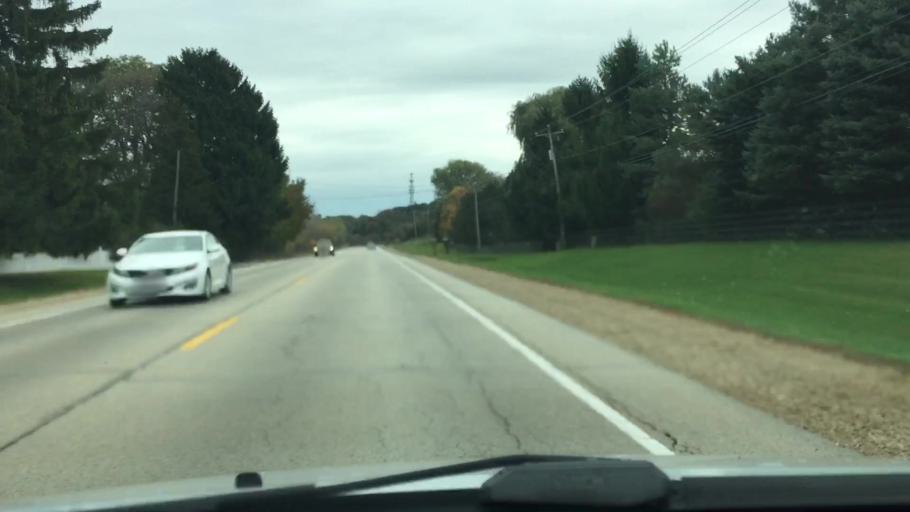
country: US
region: Wisconsin
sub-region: Waukesha County
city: Wales
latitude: 43.0204
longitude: -88.3351
